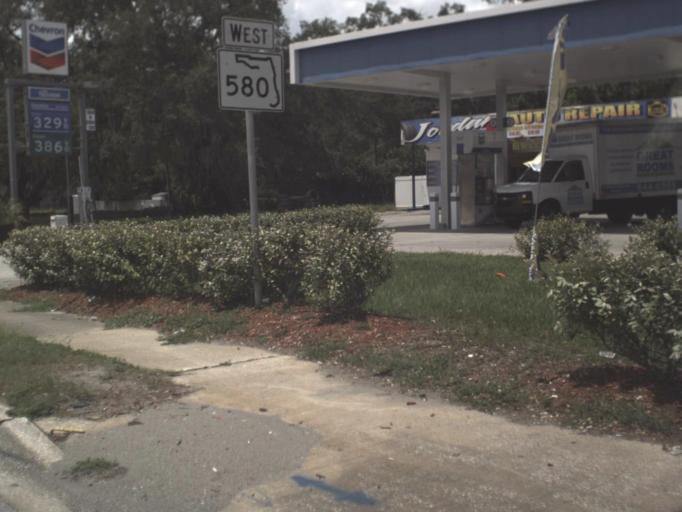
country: US
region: Florida
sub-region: Hillsborough County
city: Carrollwood
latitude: 28.0334
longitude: -82.4682
